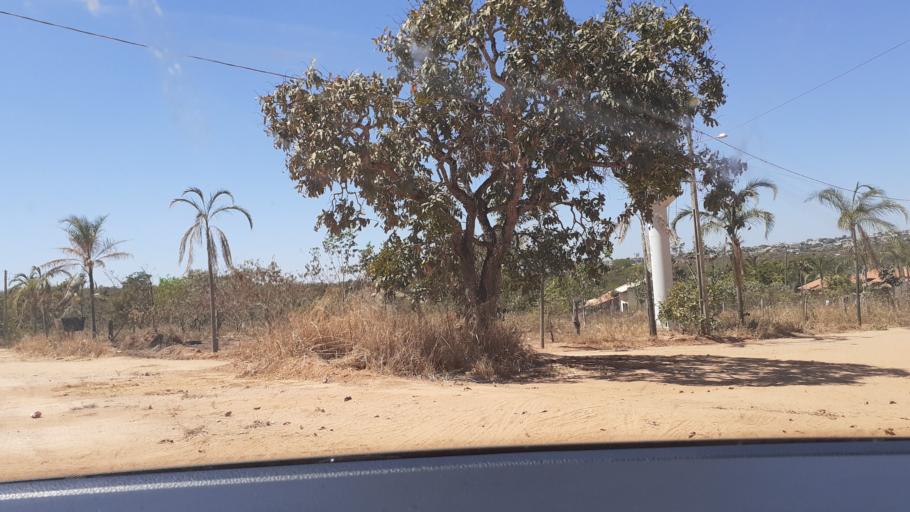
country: BR
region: Goias
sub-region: Caldas Novas
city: Caldas Novas
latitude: -17.7451
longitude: -48.6558
